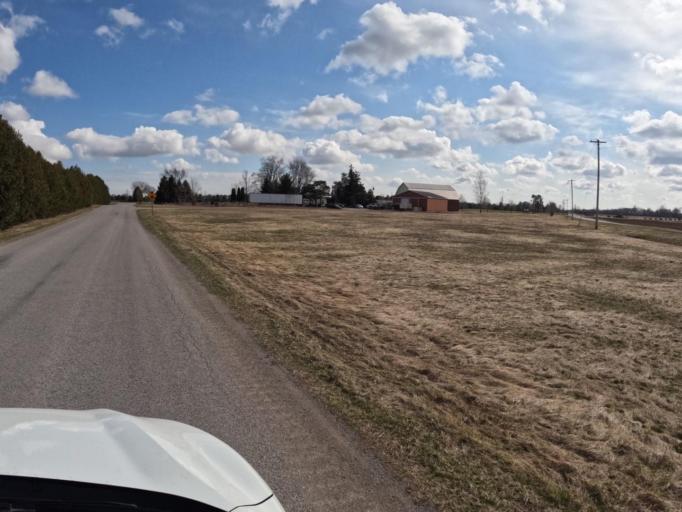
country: CA
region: Ontario
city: Norfolk County
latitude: 42.9018
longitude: -80.2895
